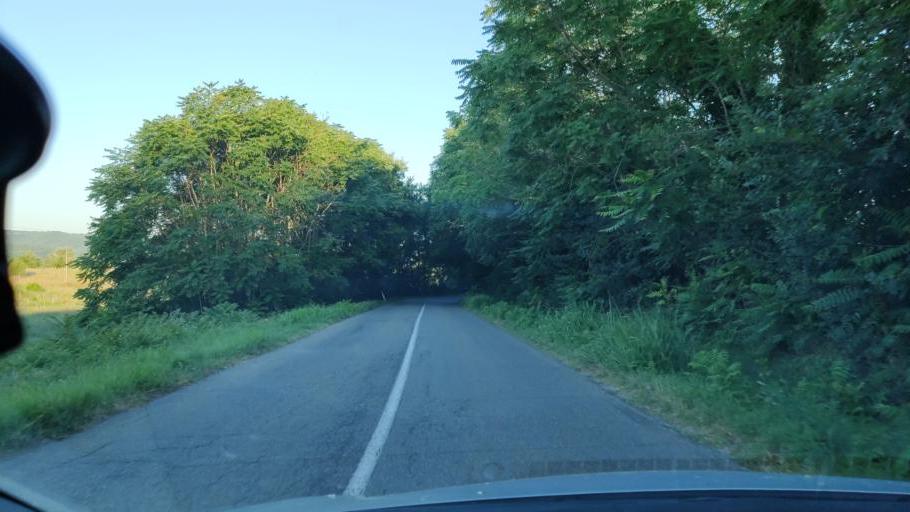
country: IT
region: Umbria
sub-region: Provincia di Terni
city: Giove
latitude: 42.5047
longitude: 12.3138
